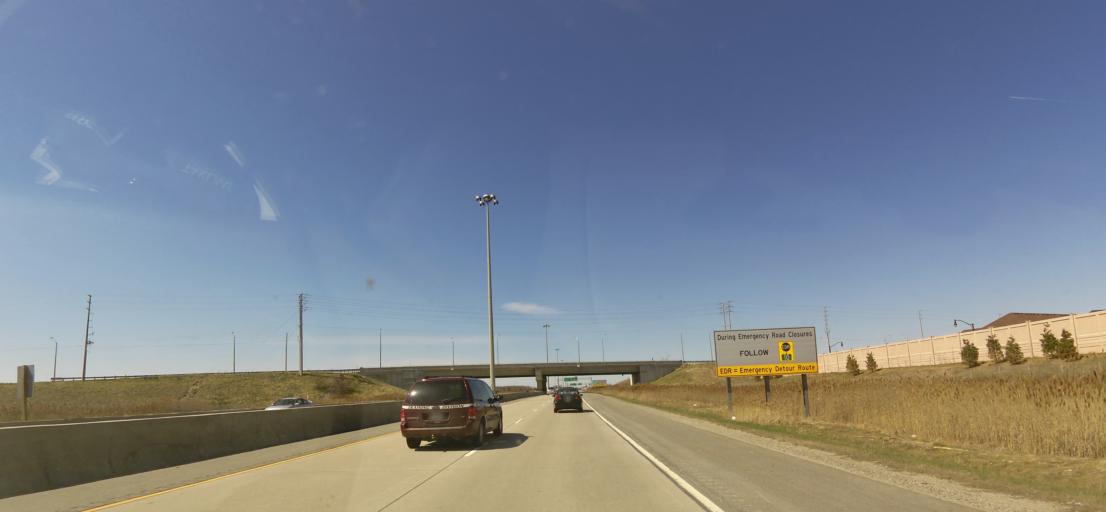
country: CA
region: Ontario
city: Brampton
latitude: 43.7467
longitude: -79.7874
